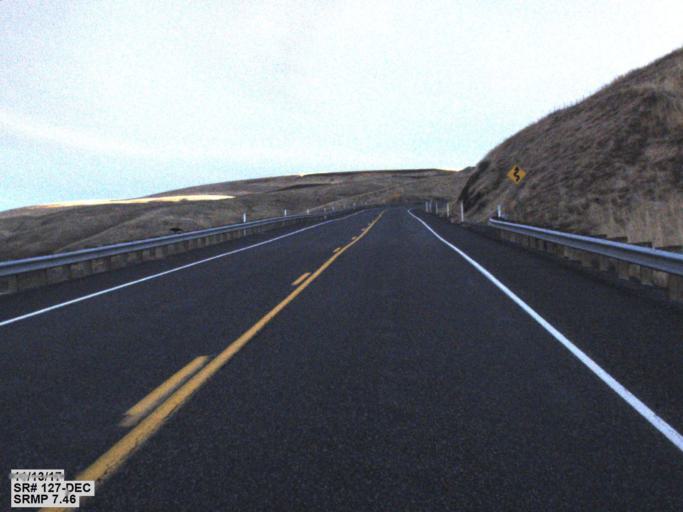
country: US
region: Washington
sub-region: Garfield County
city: Pomeroy
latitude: 46.5943
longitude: -117.7824
